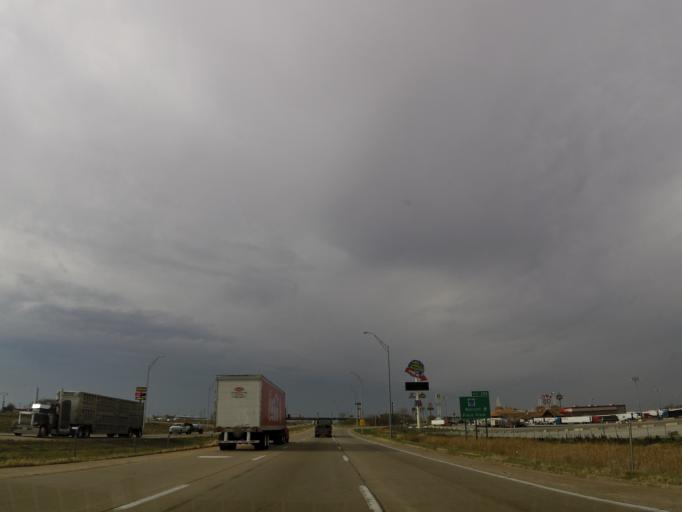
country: US
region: Iowa
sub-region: Scott County
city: Walcott
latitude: 41.6154
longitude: -90.7769
